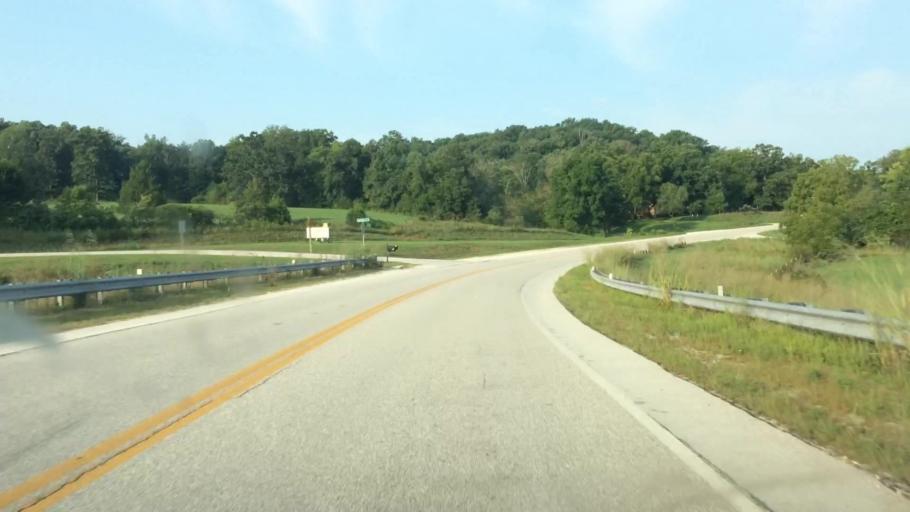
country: US
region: Missouri
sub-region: Greene County
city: Strafford
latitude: 37.1914
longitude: -93.1057
